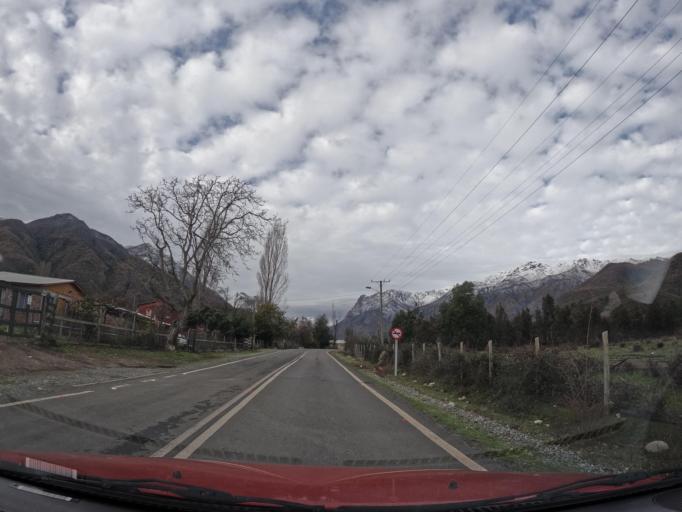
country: CL
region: Maule
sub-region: Provincia de Linares
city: Colbun
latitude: -35.8605
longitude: -71.2619
